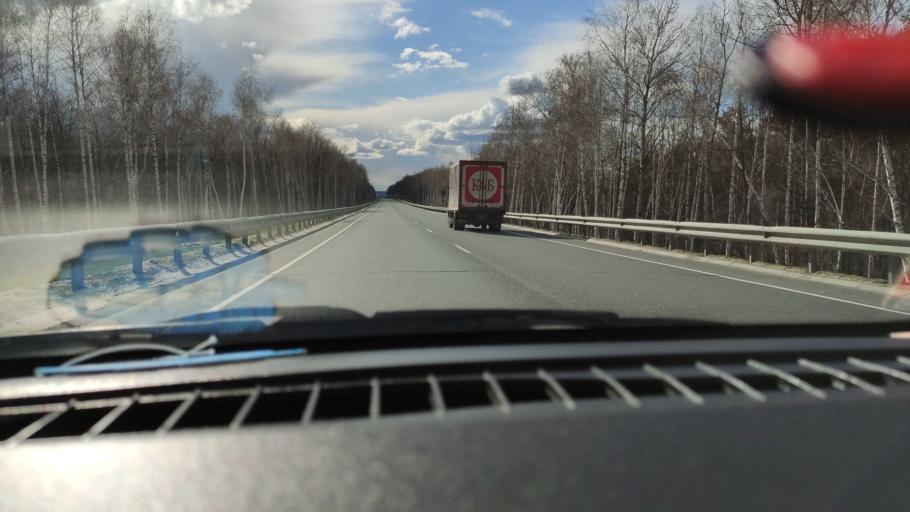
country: RU
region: Saratov
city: Vol'sk
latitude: 52.1112
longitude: 47.3392
